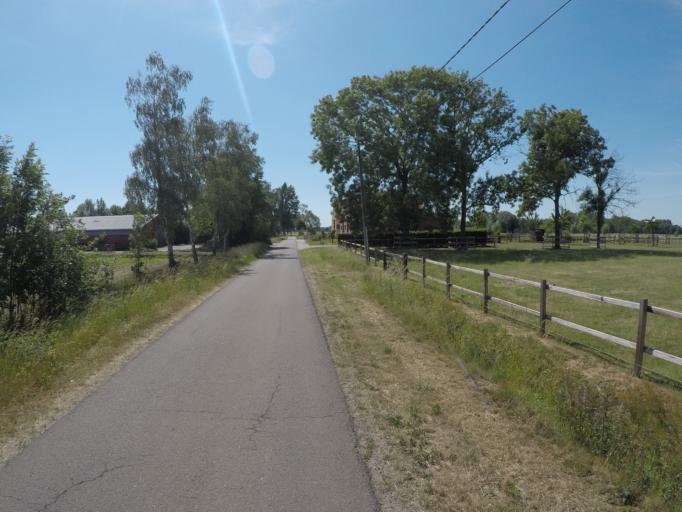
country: BE
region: Flanders
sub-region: Provincie Antwerpen
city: Wuustwezel
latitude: 51.4147
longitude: 4.6323
